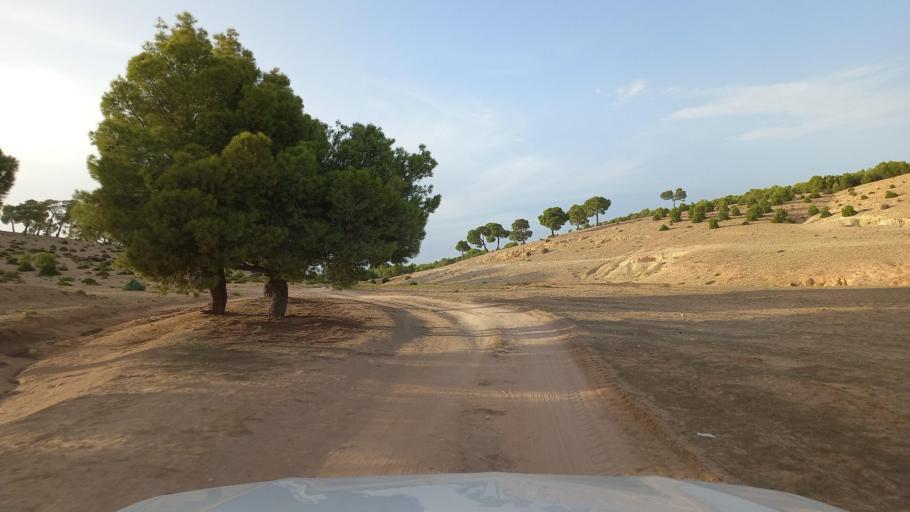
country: TN
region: Al Qasrayn
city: Sbiba
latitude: 35.4099
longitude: 8.8983
